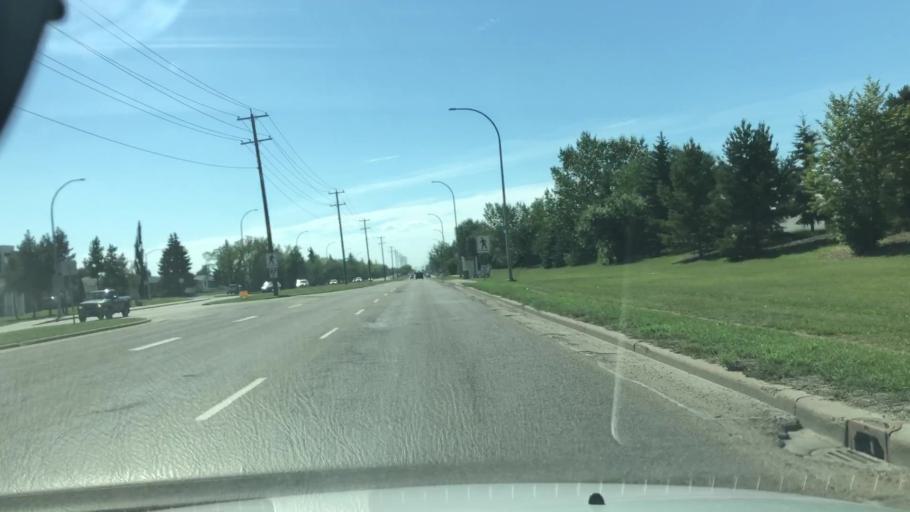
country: CA
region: Alberta
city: Edmonton
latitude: 53.5996
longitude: -113.5261
